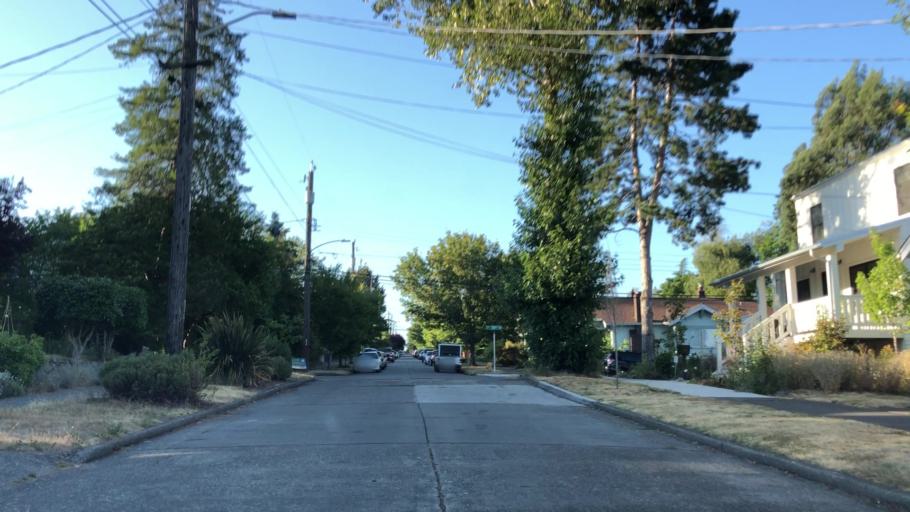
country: US
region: Washington
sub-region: King County
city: Seattle
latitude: 47.6538
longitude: -122.3351
